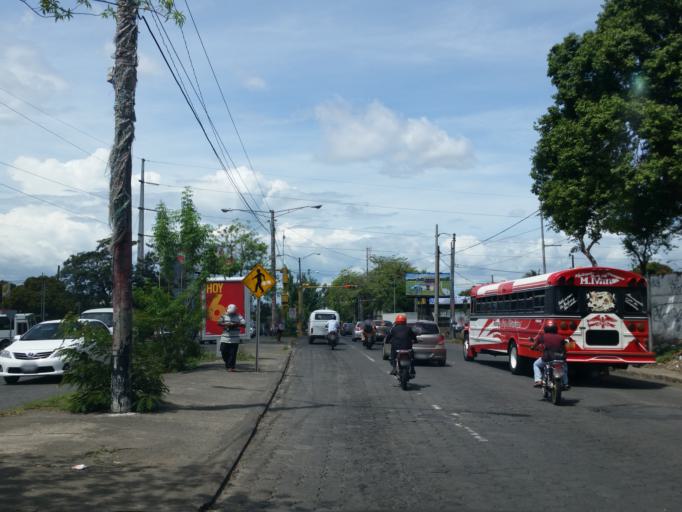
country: NI
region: Managua
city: Managua
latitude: 12.1299
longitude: -86.2315
